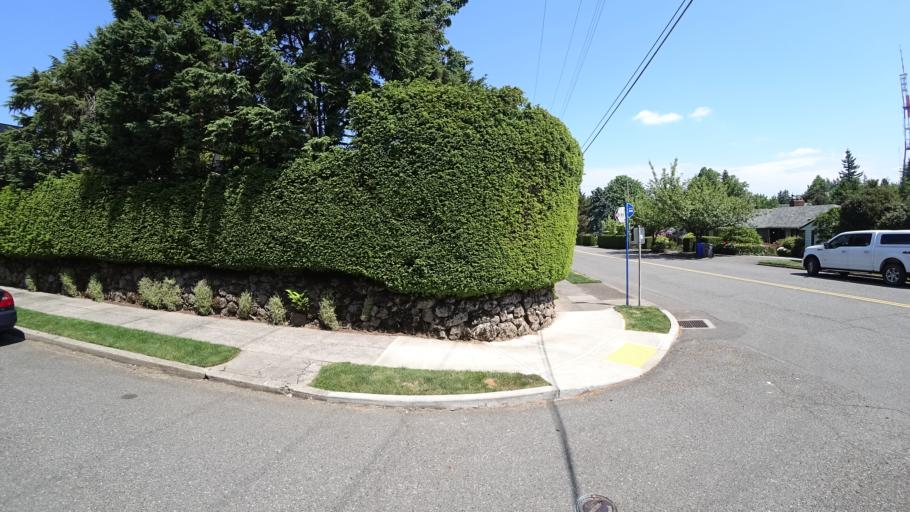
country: US
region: Oregon
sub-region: Multnomah County
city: Portland
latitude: 45.4935
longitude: -122.7007
